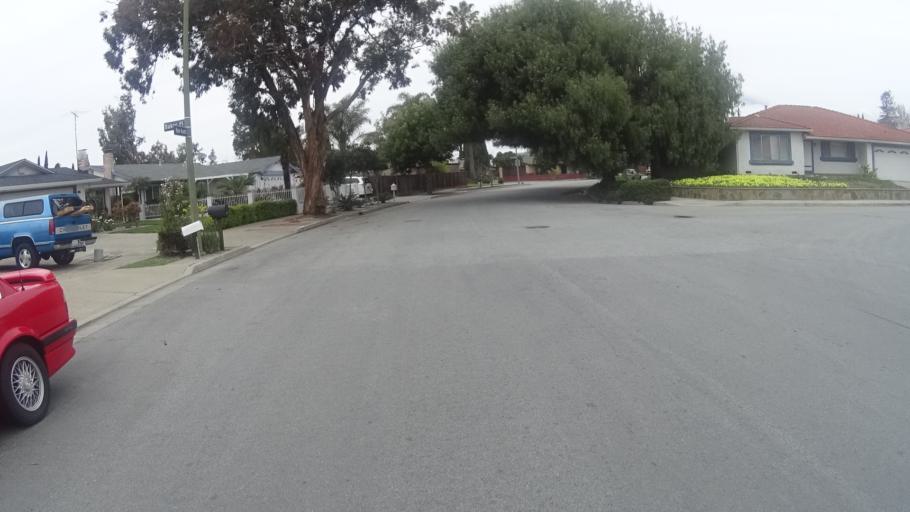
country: US
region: California
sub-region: Santa Clara County
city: San Jose
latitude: 37.3844
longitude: -121.8794
